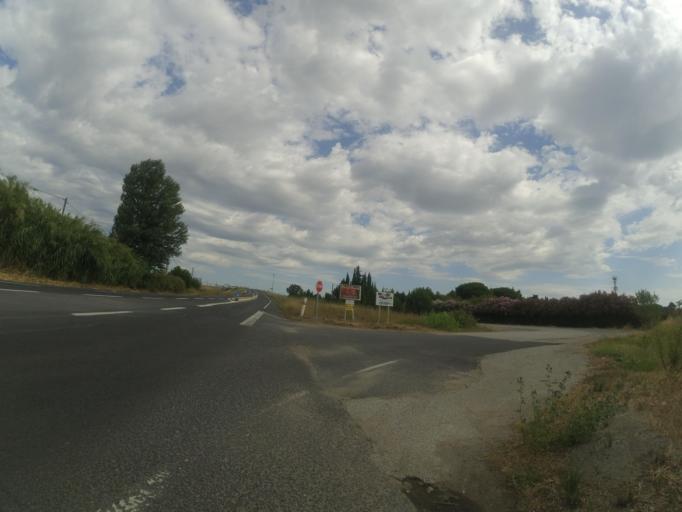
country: FR
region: Languedoc-Roussillon
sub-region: Departement des Pyrenees-Orientales
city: Toulouges
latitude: 42.6773
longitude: 2.8238
